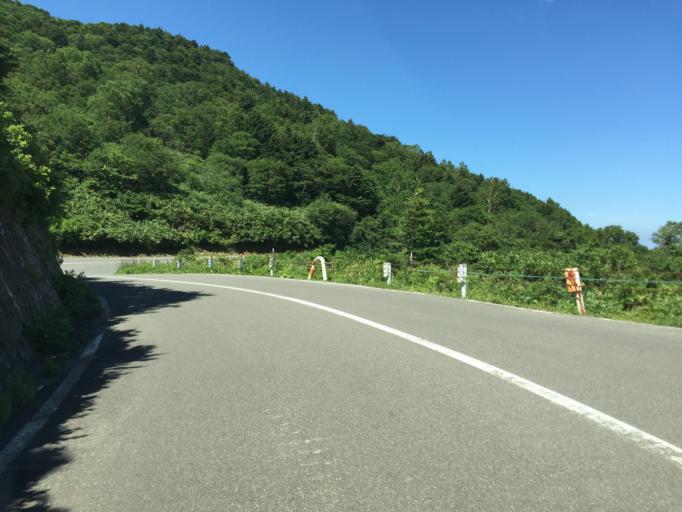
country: JP
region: Fukushima
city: Fukushima-shi
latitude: 37.7400
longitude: 140.2700
